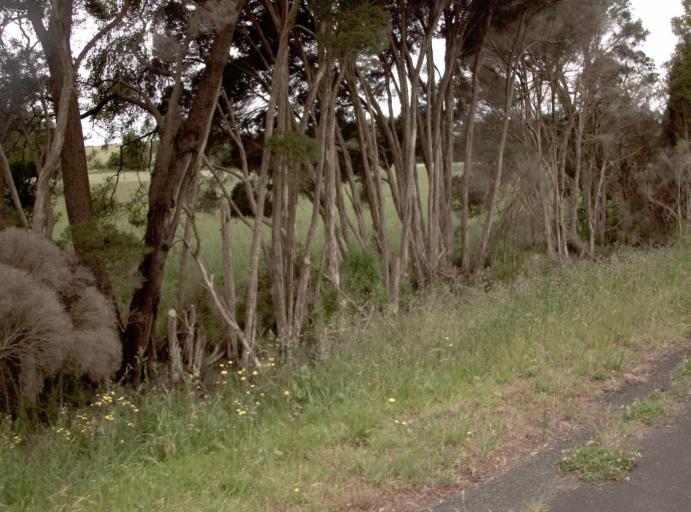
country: AU
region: Victoria
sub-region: Latrobe
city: Moe
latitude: -38.5947
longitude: 146.0986
